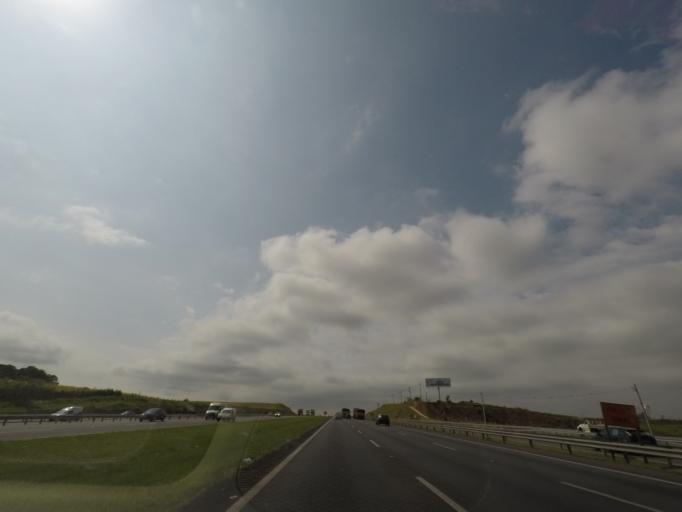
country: BR
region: Sao Paulo
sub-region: Campinas
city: Campinas
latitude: -22.8702
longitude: -47.0189
